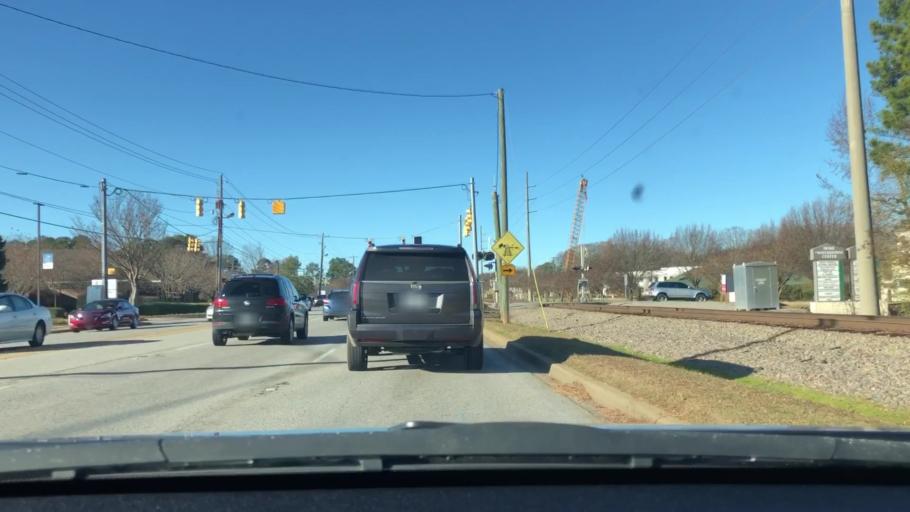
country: US
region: South Carolina
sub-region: Lexington County
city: Irmo
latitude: 34.0778
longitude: -81.1787
